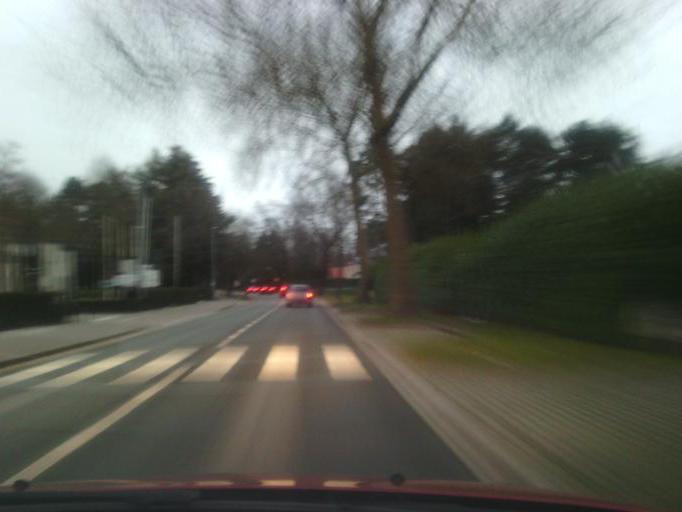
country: BE
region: Flanders
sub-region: Provincie Oost-Vlaanderen
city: Waasmunster
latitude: 51.1163
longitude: 4.1036
